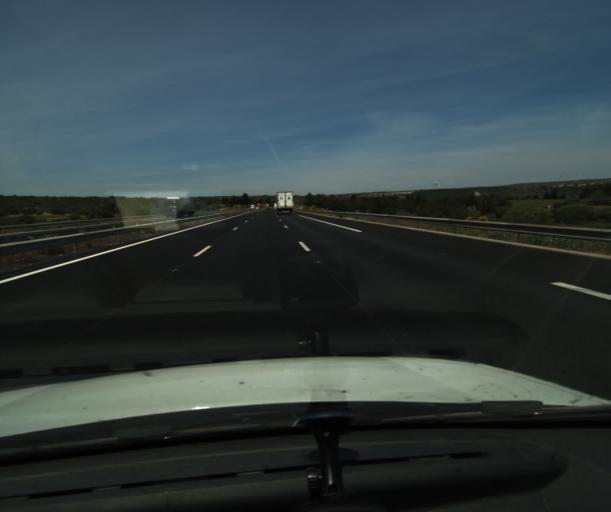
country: FR
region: Languedoc-Roussillon
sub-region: Departement de l'Aude
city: Sigean
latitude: 42.9627
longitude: 2.9691
